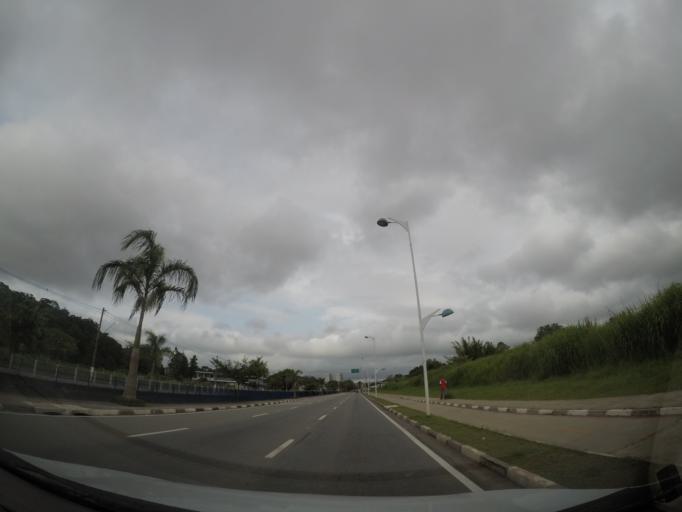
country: BR
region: Sao Paulo
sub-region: Aruja
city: Aruja
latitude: -23.3978
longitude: -46.3363
